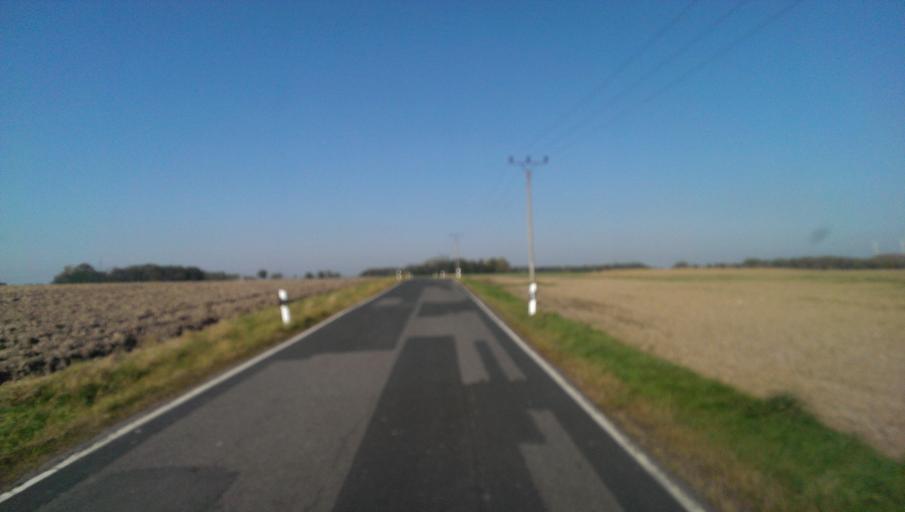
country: DE
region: Saxony
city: Stauchitz
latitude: 51.2441
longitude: 13.1880
